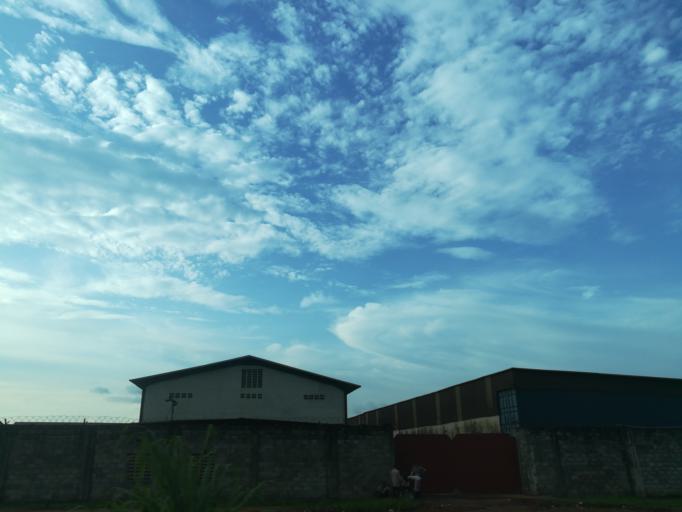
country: NG
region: Lagos
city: Ebute Ikorodu
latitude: 6.6214
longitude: 3.4519
